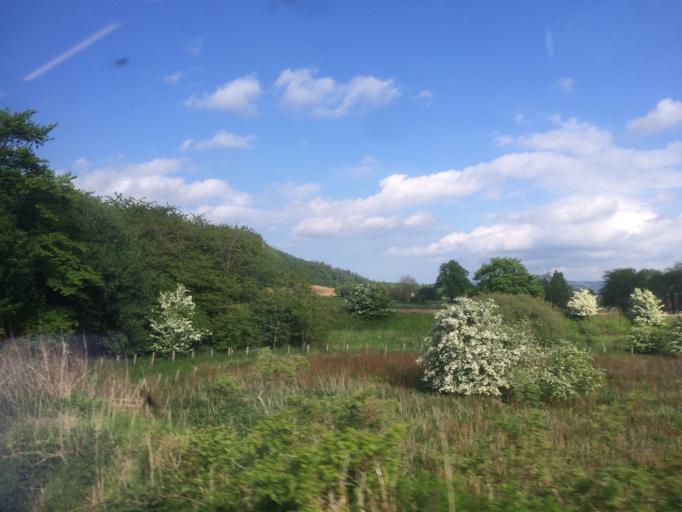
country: GB
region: Scotland
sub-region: Perth and Kinross
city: Bridge of Earn
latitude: 56.3631
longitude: -3.4340
